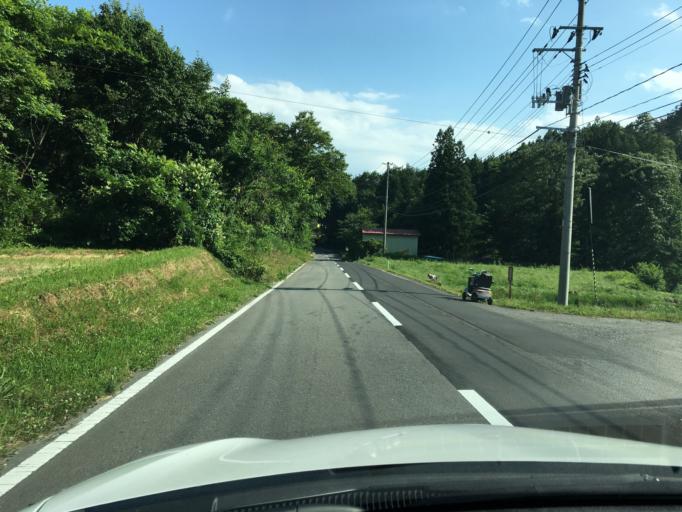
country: JP
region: Fukushima
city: Ishikawa
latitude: 37.2284
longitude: 140.5449
